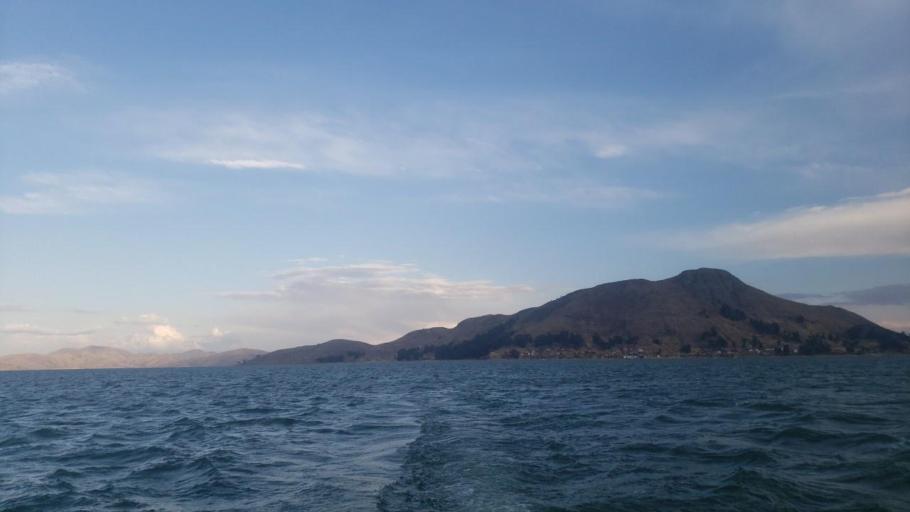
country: BO
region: La Paz
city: San Pedro
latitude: -16.2795
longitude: -68.7809
